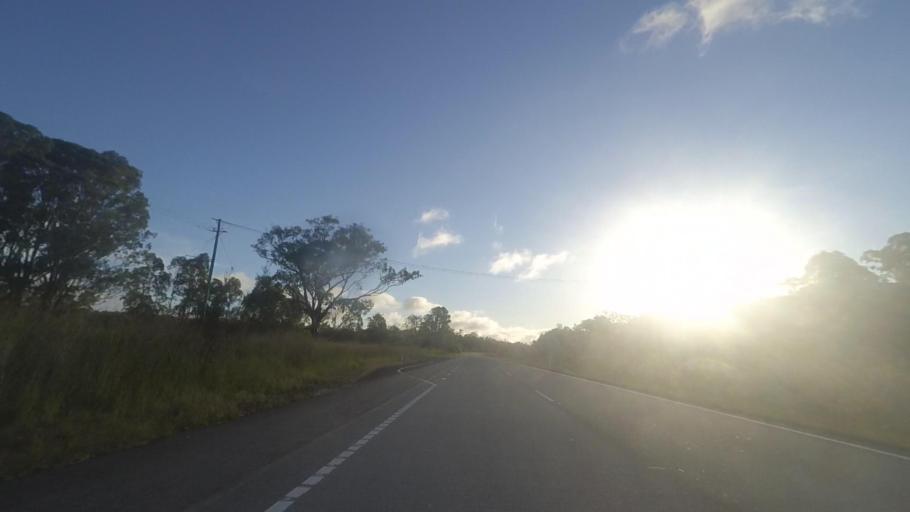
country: AU
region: New South Wales
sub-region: Great Lakes
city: Hawks Nest
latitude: -32.5434
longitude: 152.1643
